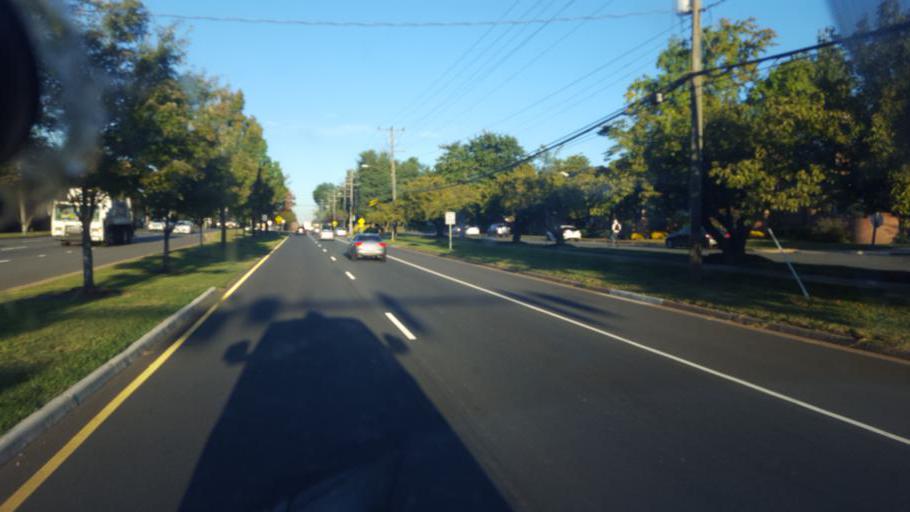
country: US
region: Virginia
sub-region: Fairfax County
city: Mantua
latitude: 38.8422
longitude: -77.2791
